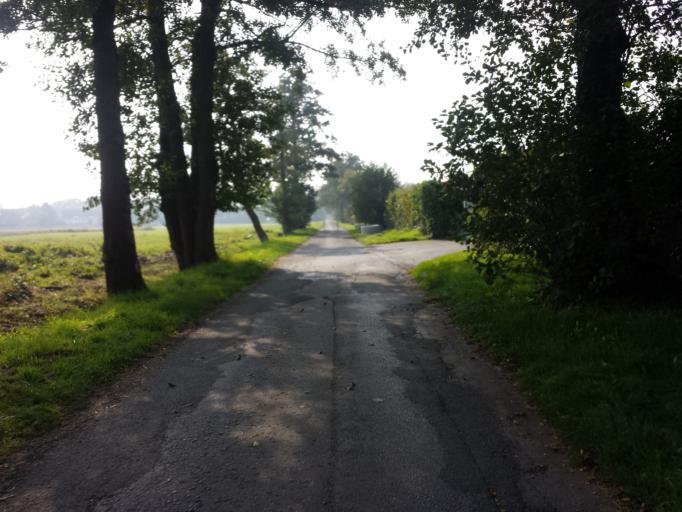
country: DE
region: North Rhine-Westphalia
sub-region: Regierungsbezirk Detmold
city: Guetersloh
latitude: 51.9175
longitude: 8.3529
